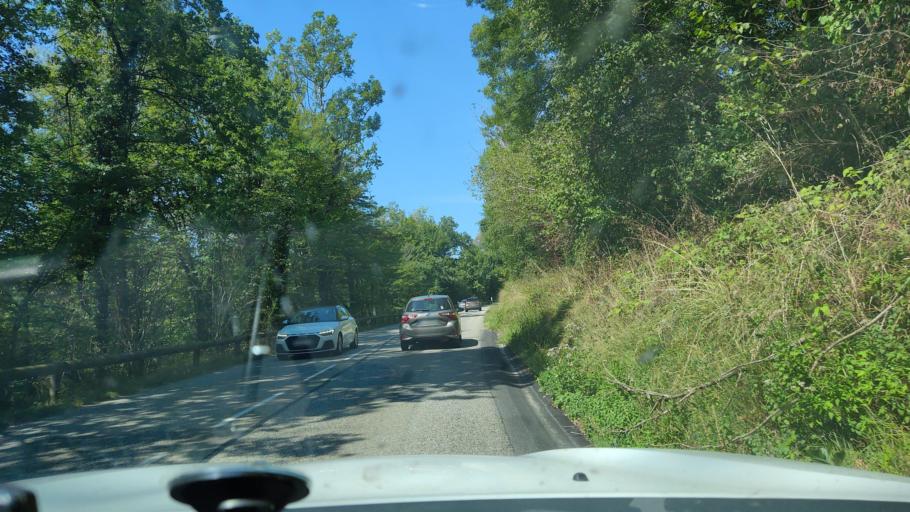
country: FR
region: Rhone-Alpes
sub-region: Departement de la Savoie
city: Novalaise
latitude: 45.5862
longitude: 5.7873
